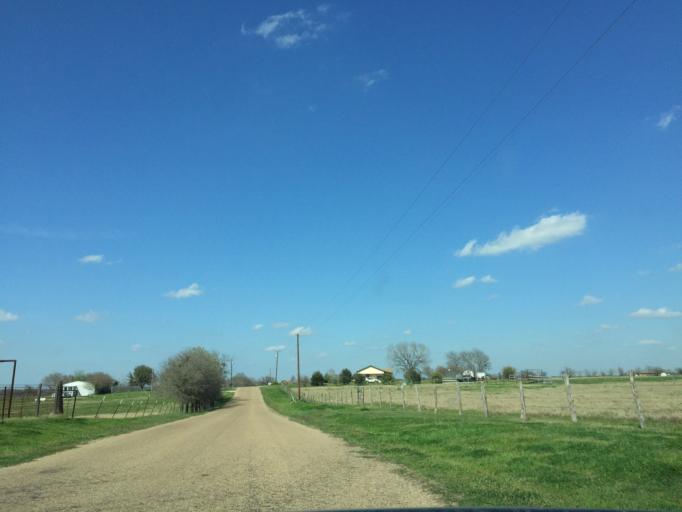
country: US
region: Texas
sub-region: Milam County
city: Thorndale
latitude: 30.5931
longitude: -97.1804
